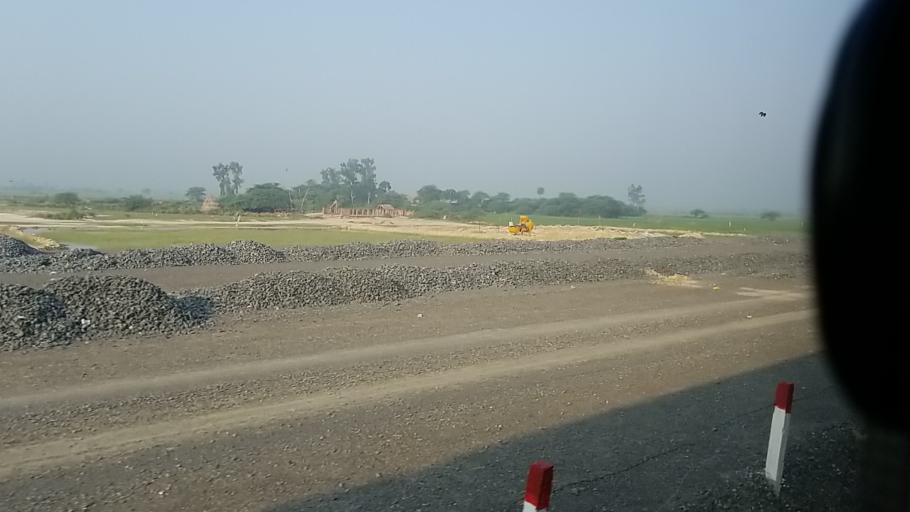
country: IN
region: Uttar Pradesh
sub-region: Auraiya
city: Phaphund
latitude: 26.6897
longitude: 79.4307
